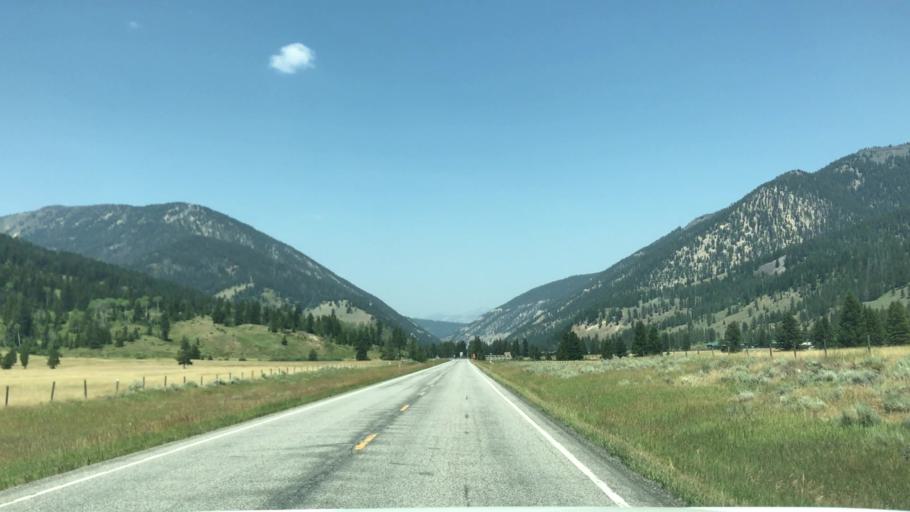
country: US
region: Montana
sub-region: Gallatin County
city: Big Sky
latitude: 45.0955
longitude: -111.2157
